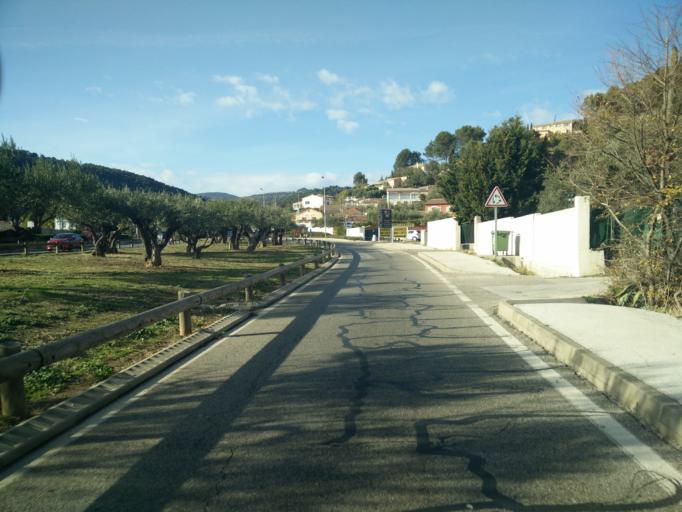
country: FR
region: Provence-Alpes-Cote d'Azur
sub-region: Departement du Var
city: Sollies-Pont
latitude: 43.1975
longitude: 6.0373
